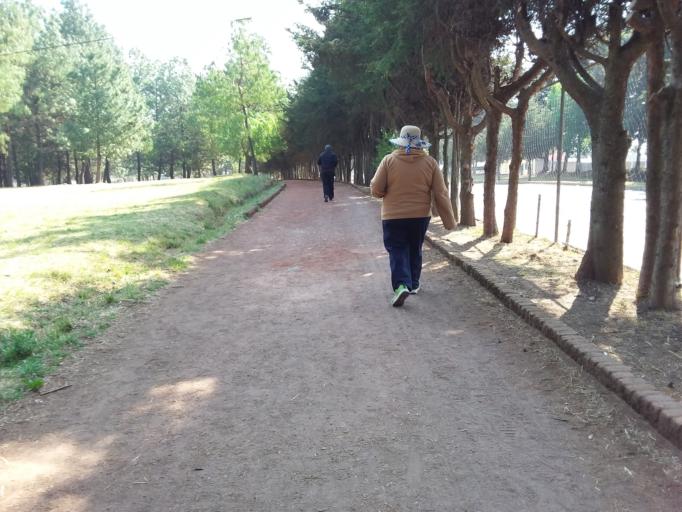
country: MX
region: Mexico
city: San Buenaventura
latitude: 19.2742
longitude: -99.6901
